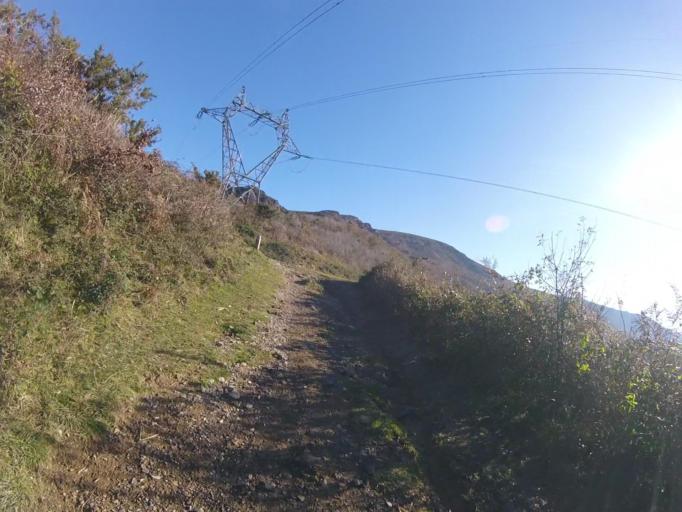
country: FR
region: Aquitaine
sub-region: Departement des Pyrenees-Atlantiques
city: Urrugne
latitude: 43.3312
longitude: -1.7343
